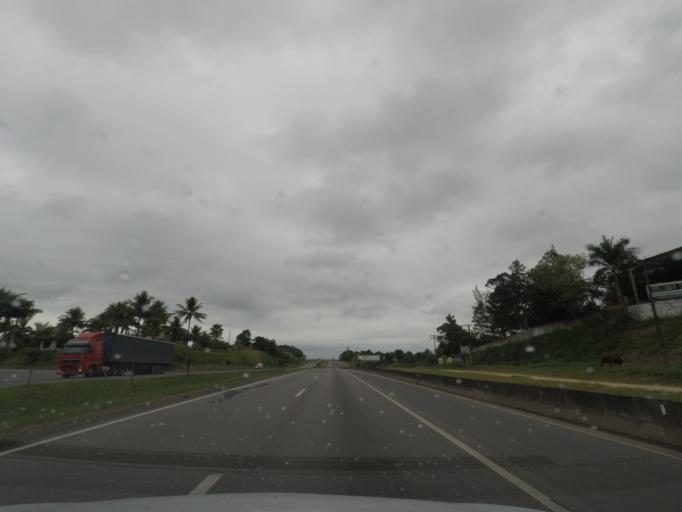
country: BR
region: Sao Paulo
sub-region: Registro
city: Registro
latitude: -24.4618
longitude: -47.8176
